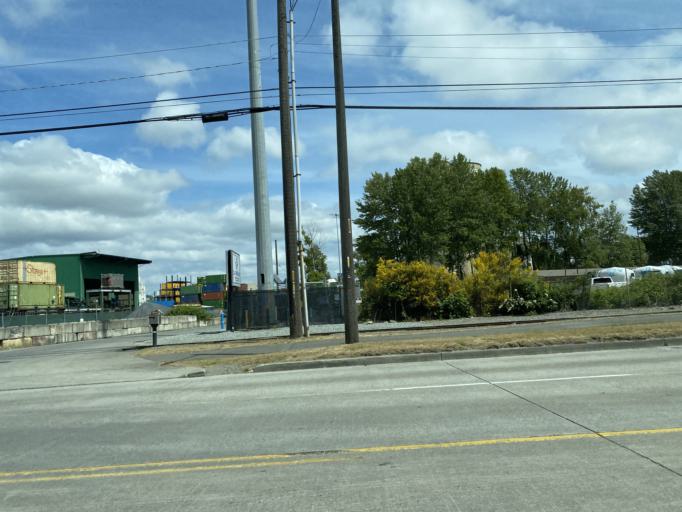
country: US
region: Washington
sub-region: King County
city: White Center
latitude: 47.5501
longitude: -122.3458
